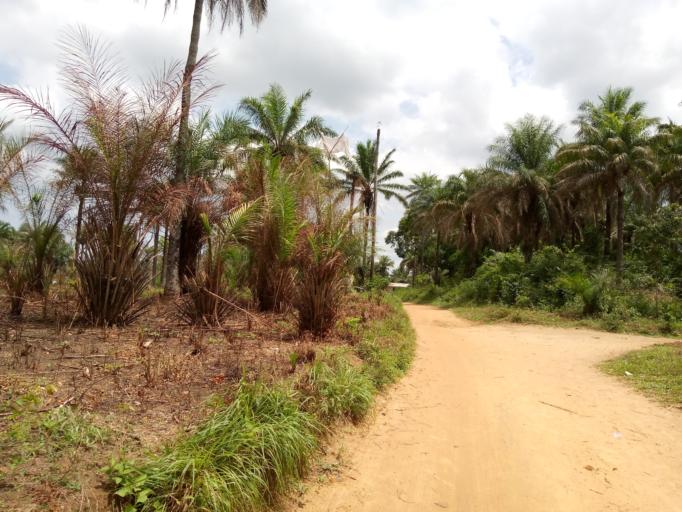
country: SL
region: Western Area
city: Waterloo
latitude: 8.4005
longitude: -12.9481
